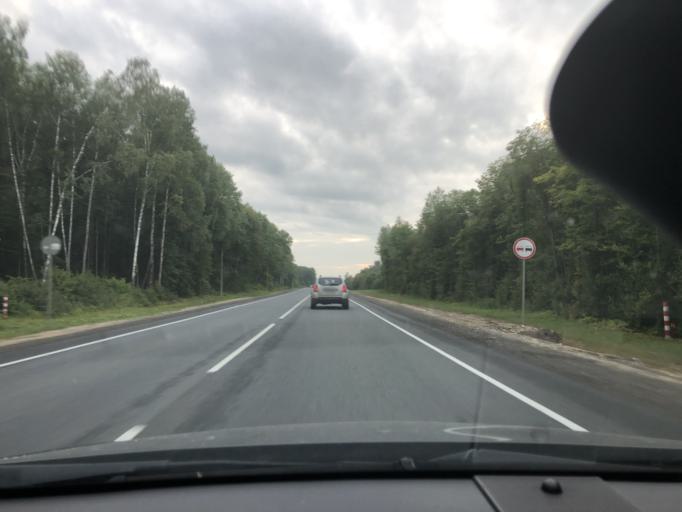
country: RU
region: Tula
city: Dubna
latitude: 54.3122
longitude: 37.0095
